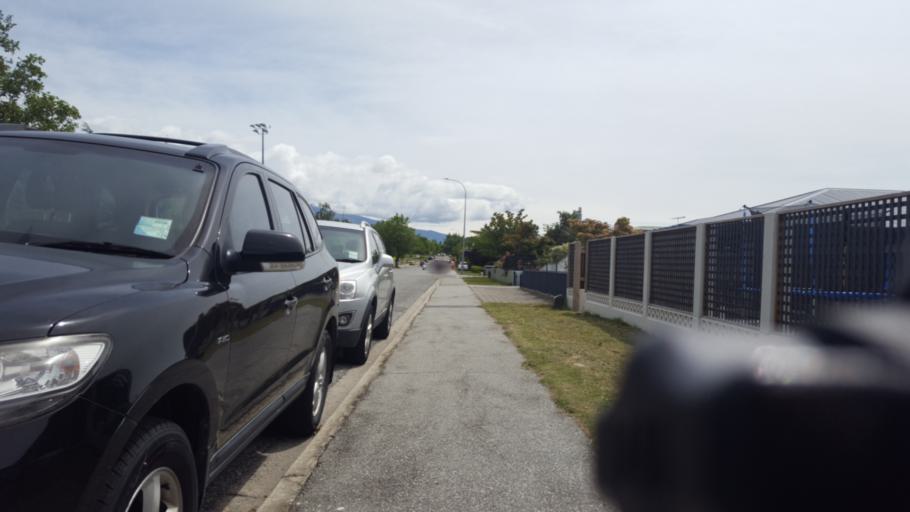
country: NZ
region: Otago
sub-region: Queenstown-Lakes District
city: Wanaka
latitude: -45.0409
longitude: 169.1975
